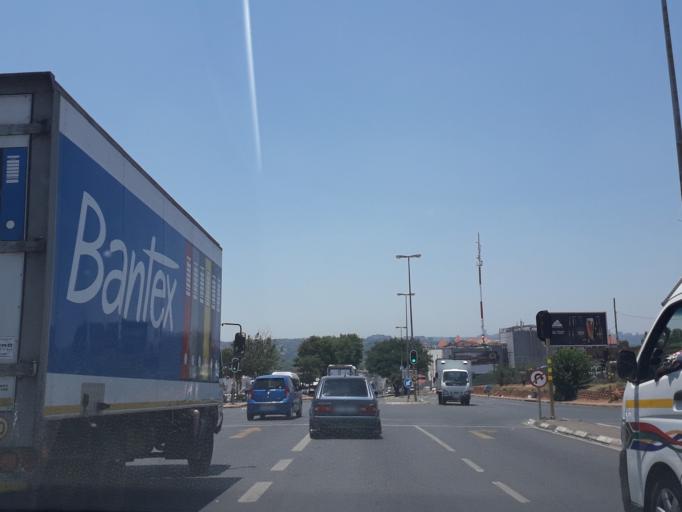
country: ZA
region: Gauteng
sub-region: City of Johannesburg Metropolitan Municipality
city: Johannesburg
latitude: -26.0953
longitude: 28.0068
